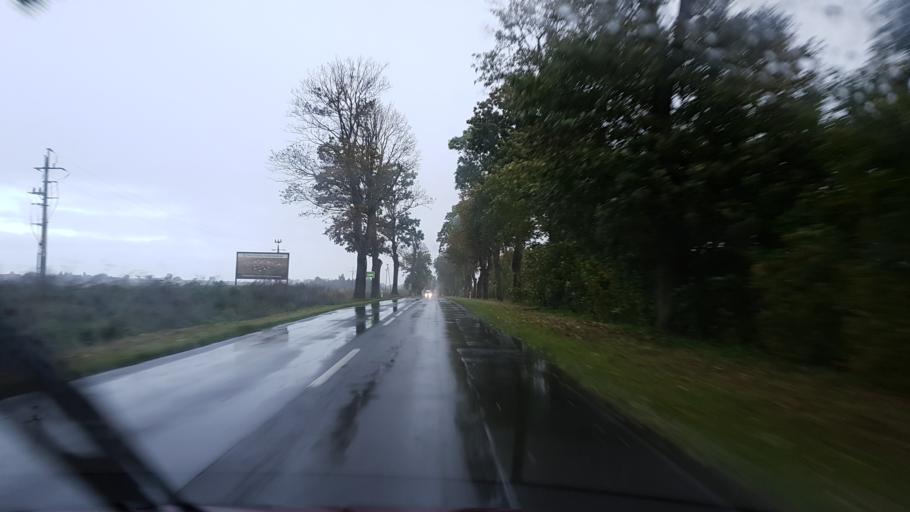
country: PL
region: Greater Poland Voivodeship
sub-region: Powiat pilski
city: Szydlowo
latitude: 53.1601
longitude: 16.6362
